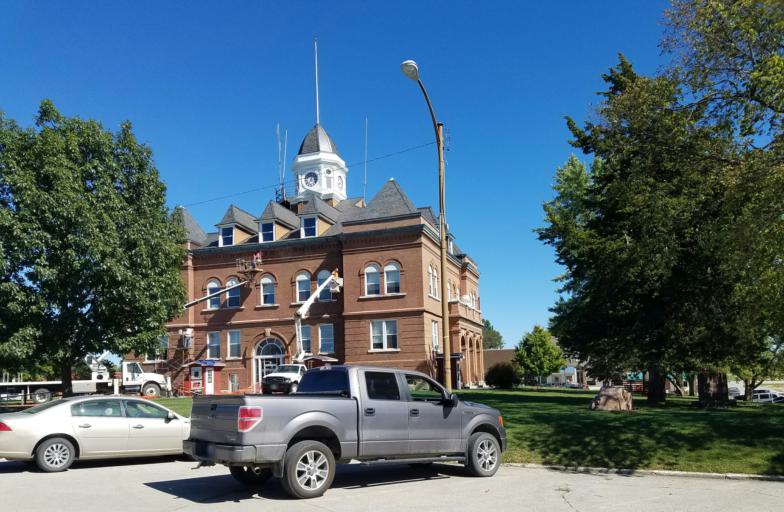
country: US
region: Missouri
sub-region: Worth County
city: Grant City
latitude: 40.4858
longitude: -94.4157
